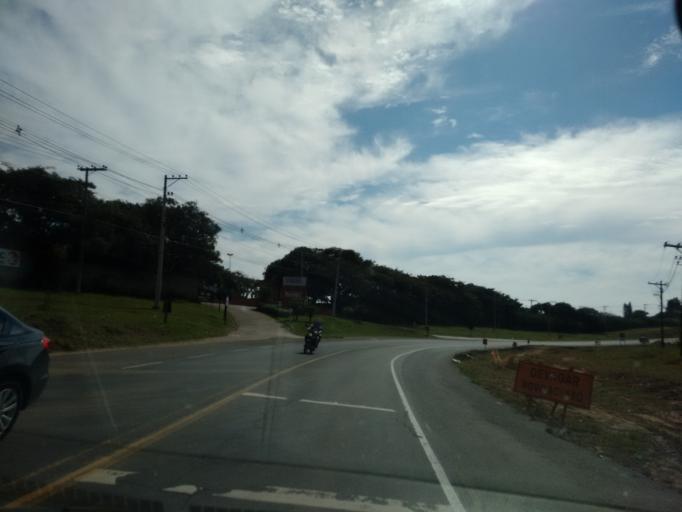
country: BR
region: Sao Paulo
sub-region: Itu
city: Itu
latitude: -23.3008
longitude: -47.3037
